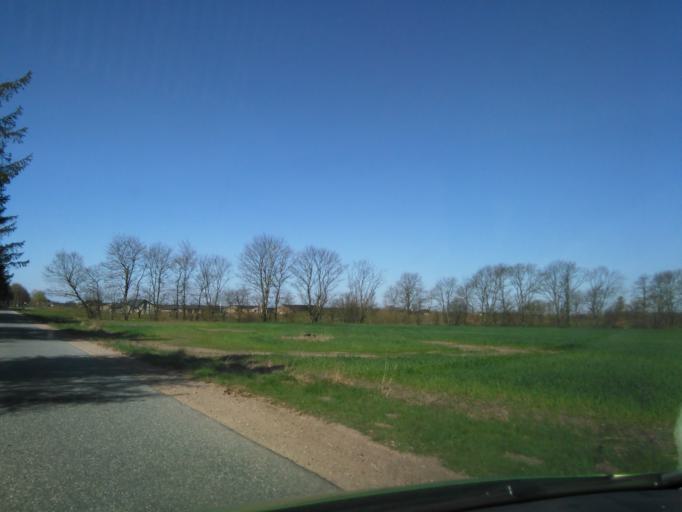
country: DK
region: South Denmark
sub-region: Billund Kommune
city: Billund
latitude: 55.7087
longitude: 9.1283
